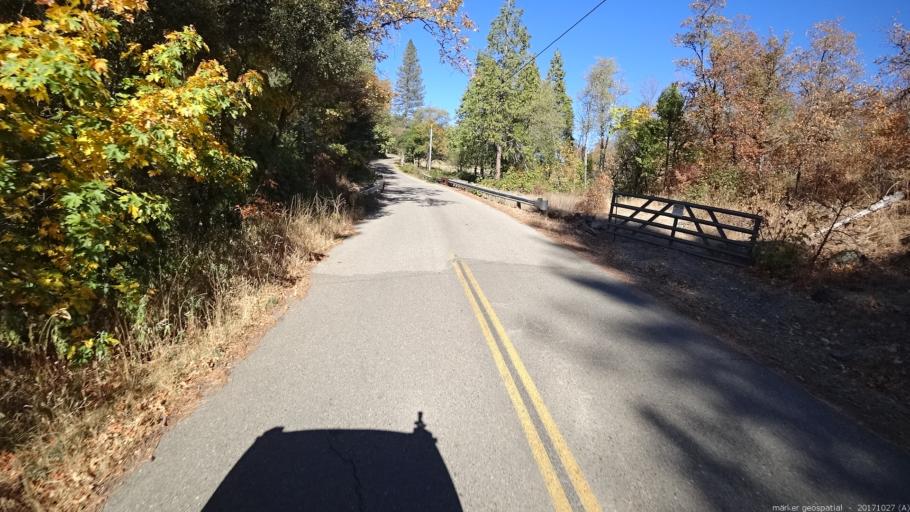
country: US
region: California
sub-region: Shasta County
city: Shingletown
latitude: 40.7135
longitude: -121.9455
